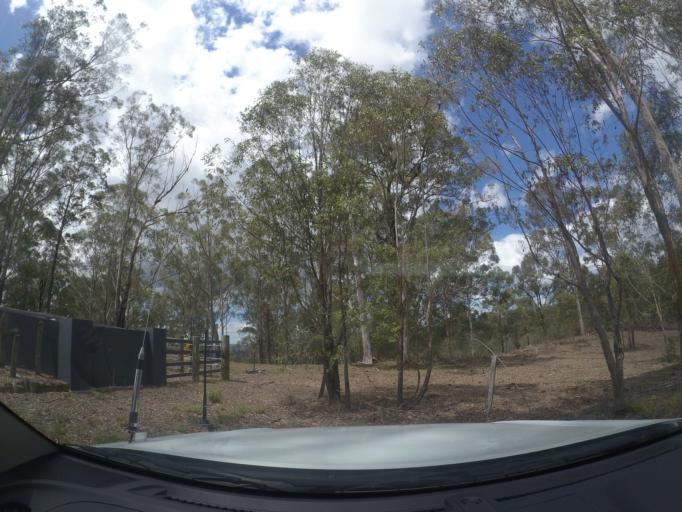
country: AU
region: Queensland
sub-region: Logan
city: Cedar Vale
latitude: -27.9165
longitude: 153.0364
